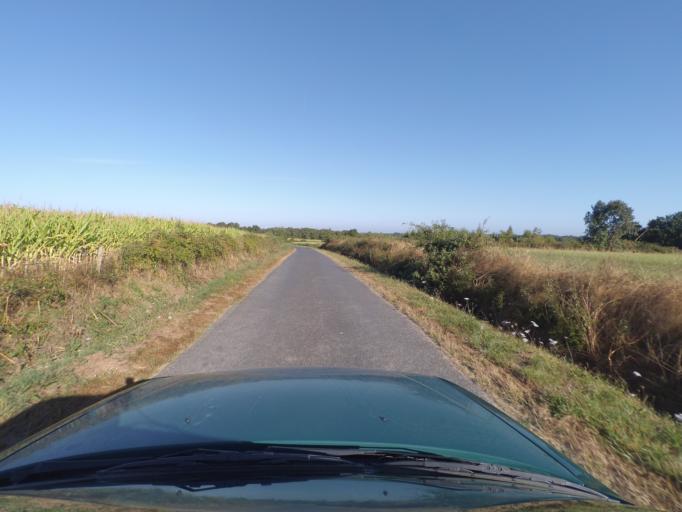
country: FR
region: Pays de la Loire
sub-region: Departement de la Loire-Atlantique
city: Le Bignon
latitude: 47.0888
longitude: -1.4618
